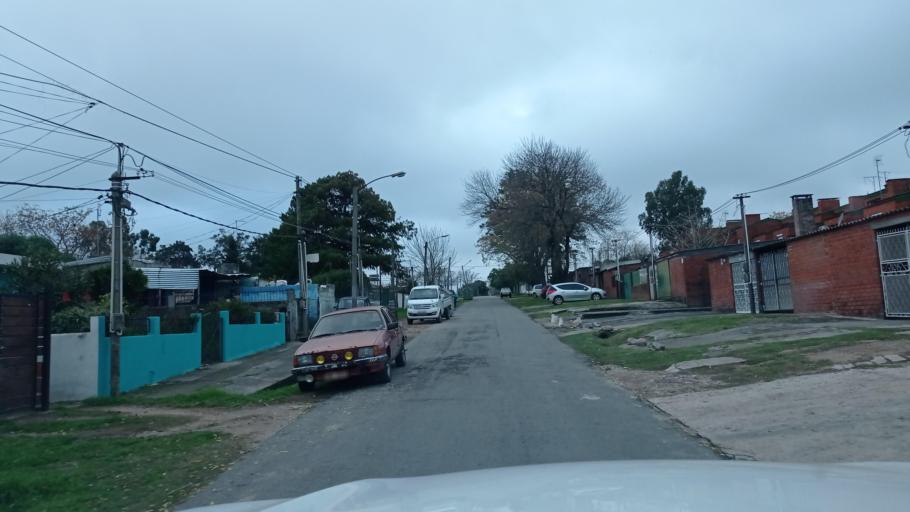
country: UY
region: Canelones
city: La Paz
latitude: -34.8378
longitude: -56.2303
